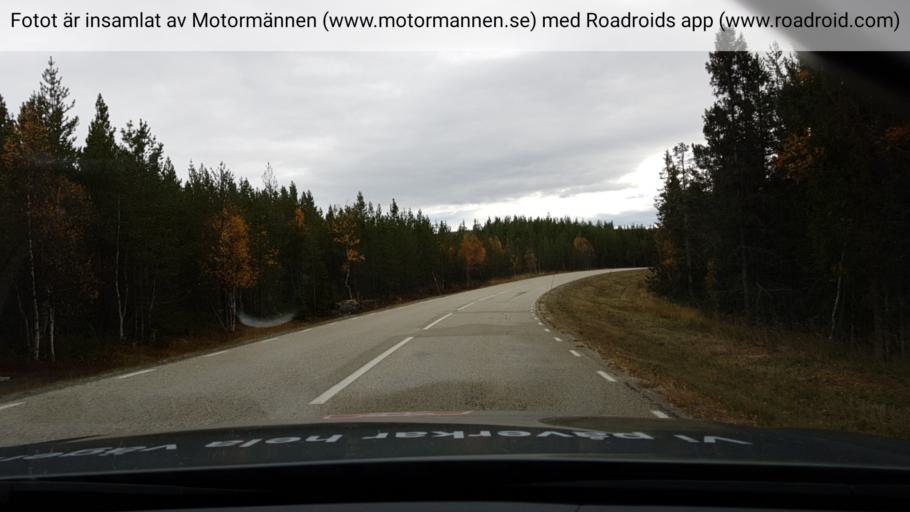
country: SE
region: Jaemtland
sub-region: Are Kommun
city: Are
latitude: 62.8225
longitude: 12.9224
